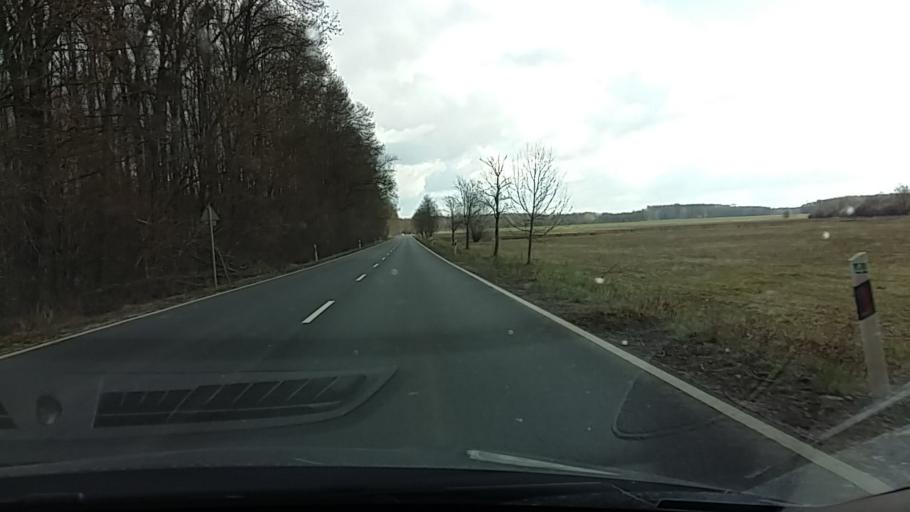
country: HU
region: Somogy
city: Bohonye
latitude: 46.4090
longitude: 17.4153
